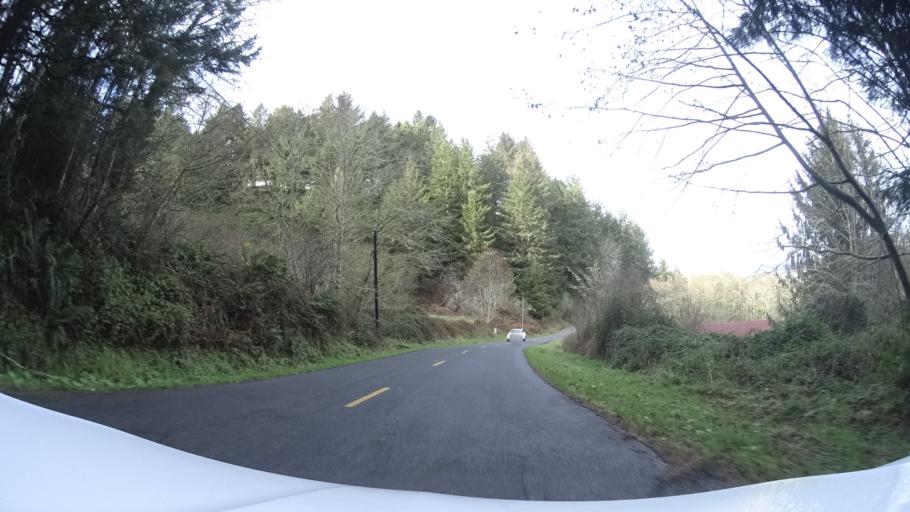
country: US
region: California
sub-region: Humboldt County
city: Ferndale
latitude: 40.5677
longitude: -124.2704
